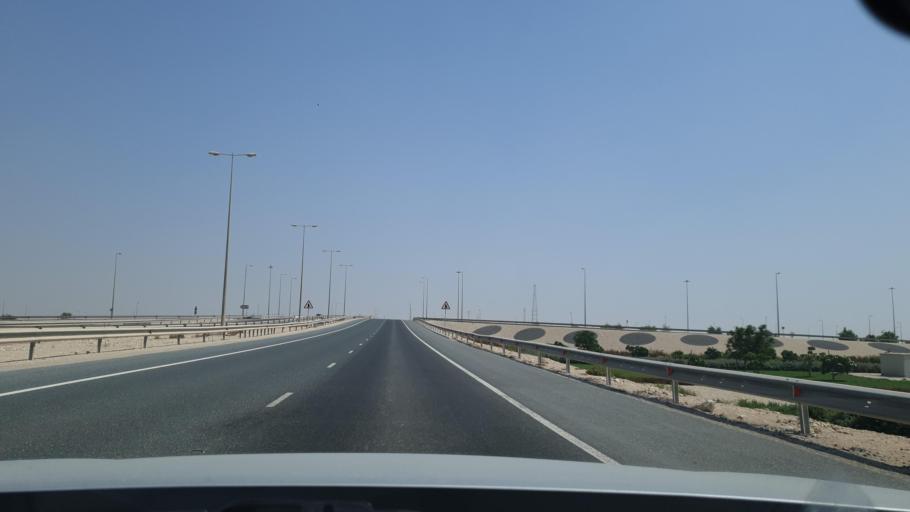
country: QA
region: Baladiyat az Za`ayin
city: Az Za`ayin
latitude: 25.6208
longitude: 51.3985
